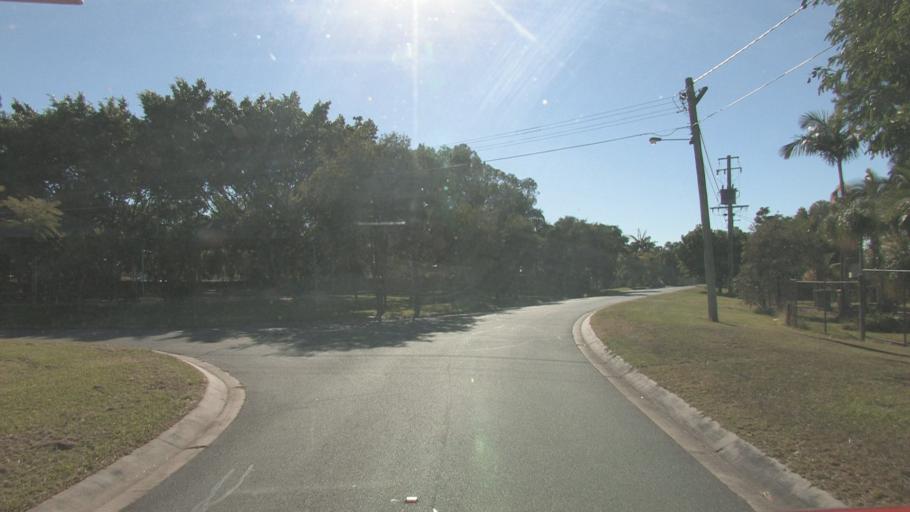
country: AU
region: Queensland
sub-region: Logan
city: Slacks Creek
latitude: -27.6525
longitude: 153.1554
